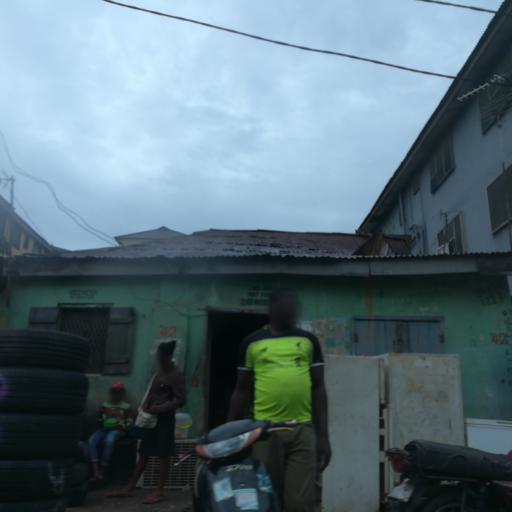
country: NG
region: Lagos
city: Makoko
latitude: 6.4923
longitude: 3.3805
